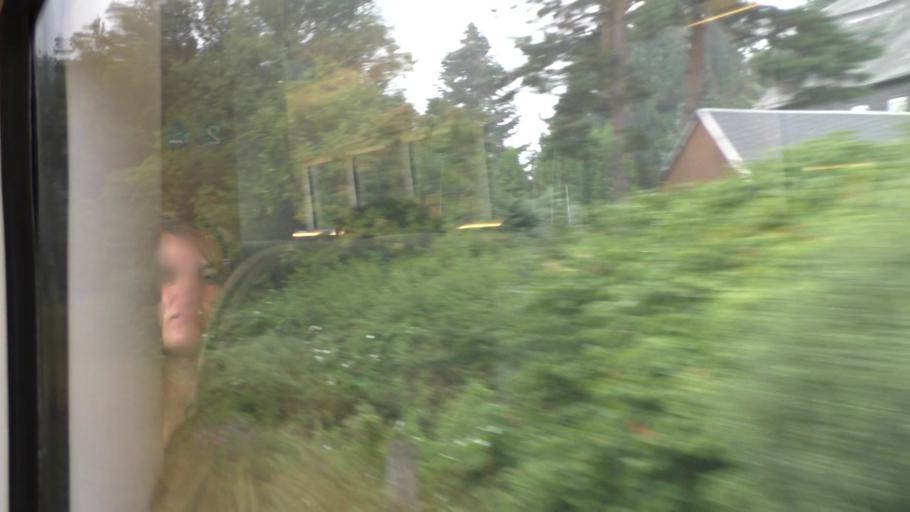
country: DE
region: Saxony
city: Neugersdorf
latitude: 50.9881
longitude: 14.5950
